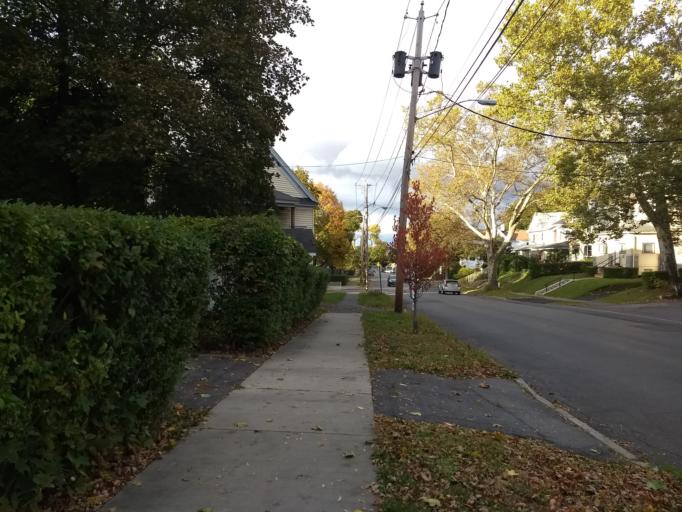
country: US
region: New York
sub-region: Onondaga County
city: Syracuse
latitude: 43.0615
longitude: -76.1360
